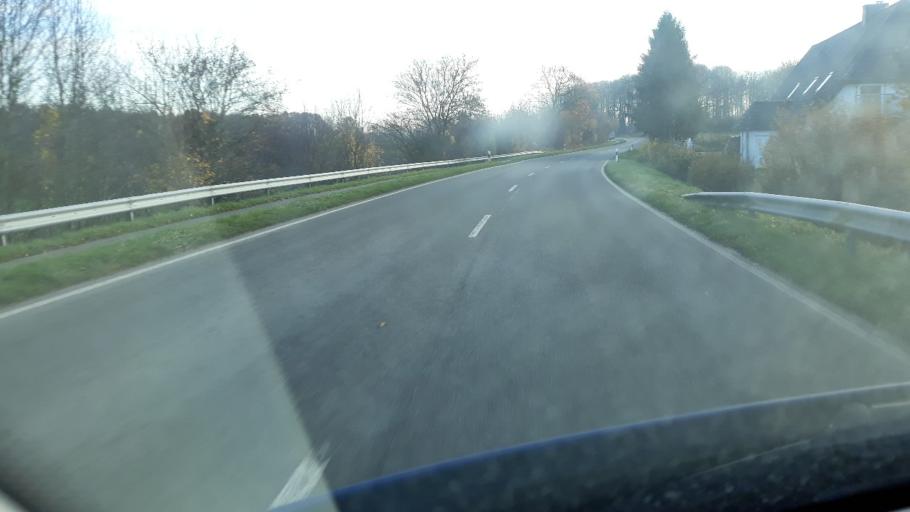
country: DE
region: Schleswig-Holstein
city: Maasholm
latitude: 54.6628
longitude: 9.9680
